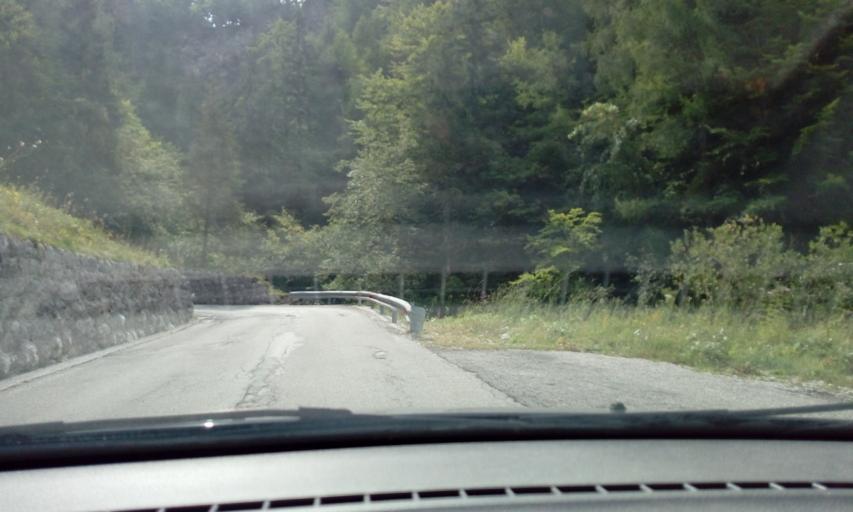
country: SI
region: Bovec
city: Bovec
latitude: 46.3903
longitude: 13.4685
